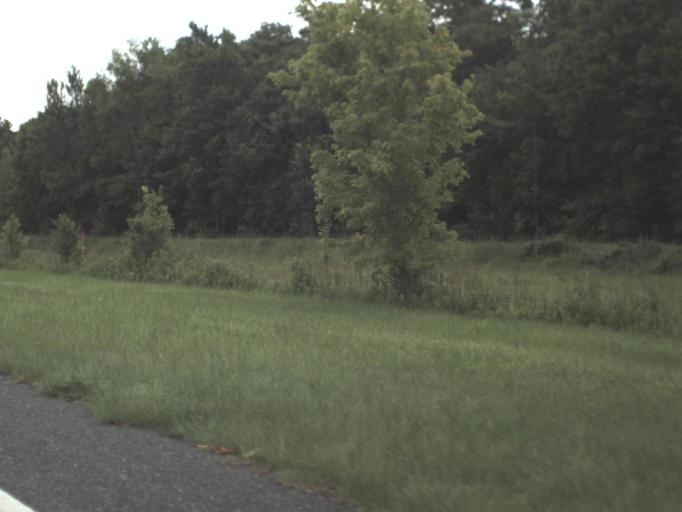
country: US
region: Florida
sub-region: Levy County
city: Williston Highlands
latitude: 29.2395
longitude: -82.7147
